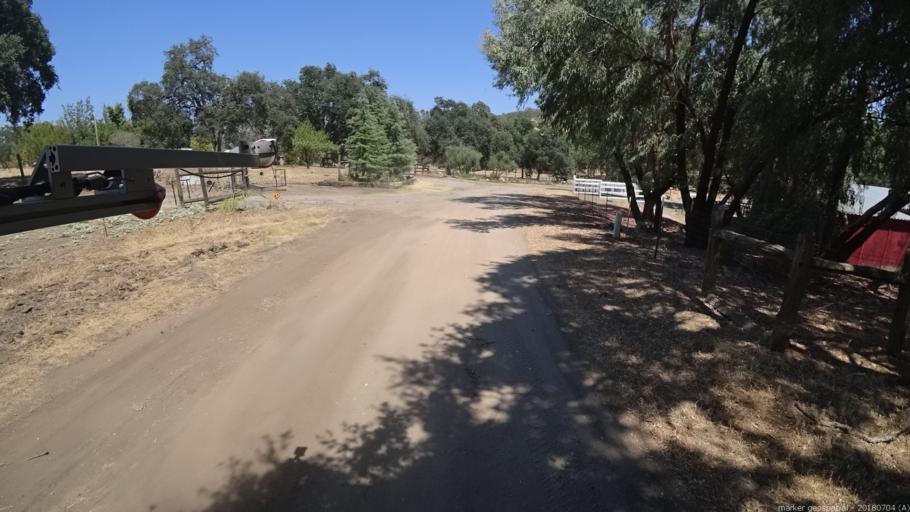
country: US
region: California
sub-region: Madera County
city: Yosemite Lakes
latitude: 37.1355
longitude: -119.6871
